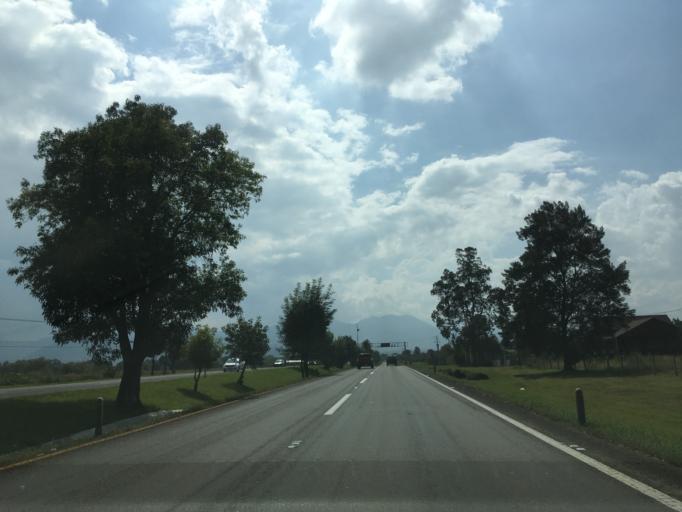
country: MX
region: Michoacan
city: Acuitzio del Canje
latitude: 19.5618
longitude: -101.3288
